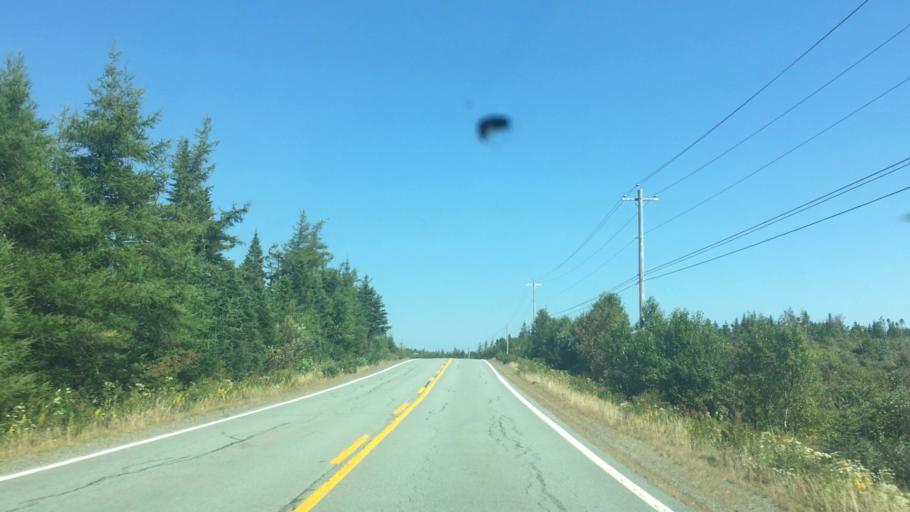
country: CA
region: Nova Scotia
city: Antigonish
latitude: 45.0193
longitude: -62.0327
